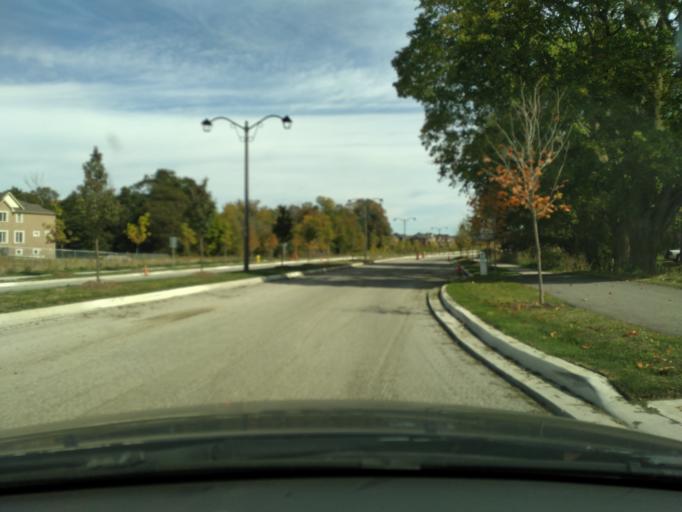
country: CA
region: Ontario
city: Oshawa
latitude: 43.9534
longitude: -78.9108
